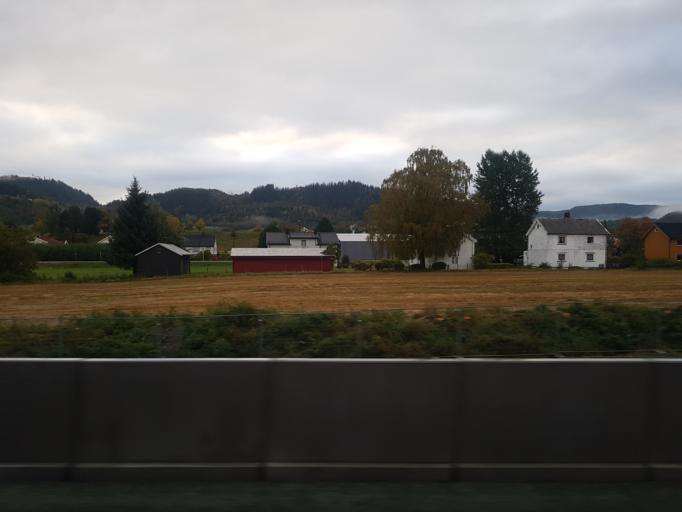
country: NO
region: Sor-Trondelag
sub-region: Melhus
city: Lundamo
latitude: 63.2052
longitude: 10.3042
